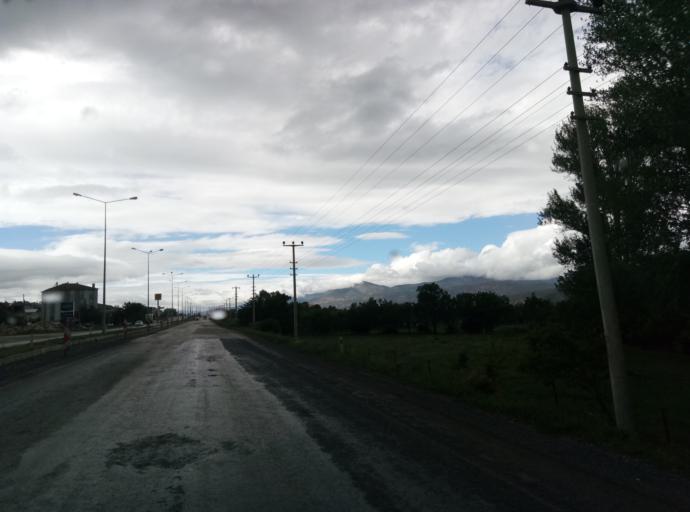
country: TR
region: Sivas
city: Susehri
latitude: 40.1716
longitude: 38.0906
